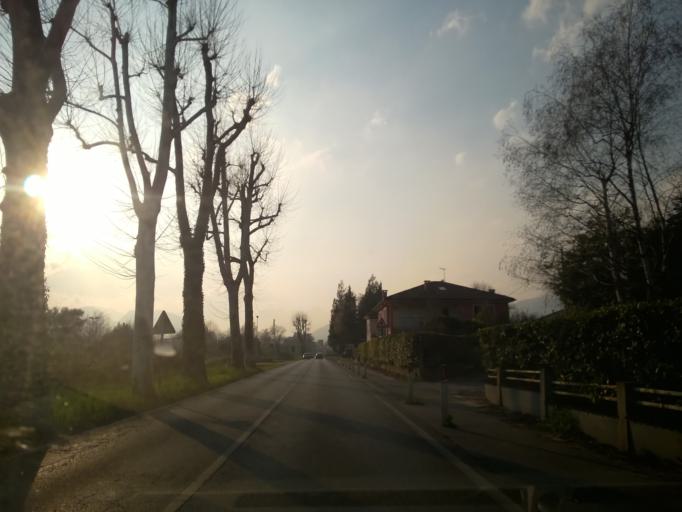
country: IT
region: Veneto
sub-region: Provincia di Vicenza
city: Giavenale
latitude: 45.7095
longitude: 11.3864
